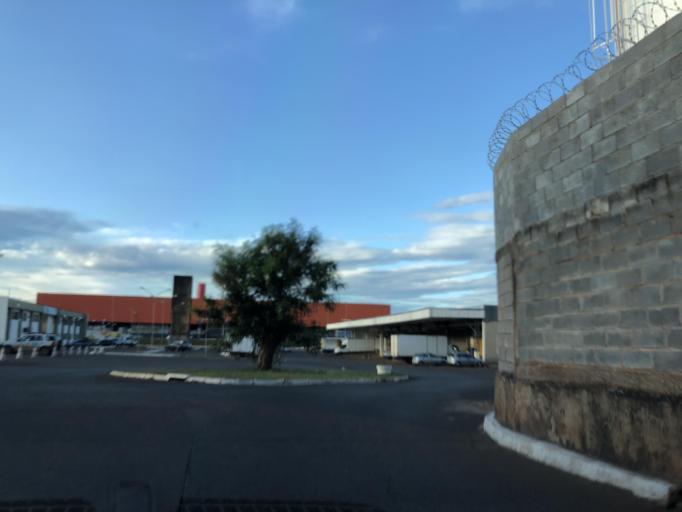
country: BR
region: Federal District
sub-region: Brasilia
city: Brasilia
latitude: -15.7929
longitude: -47.9469
